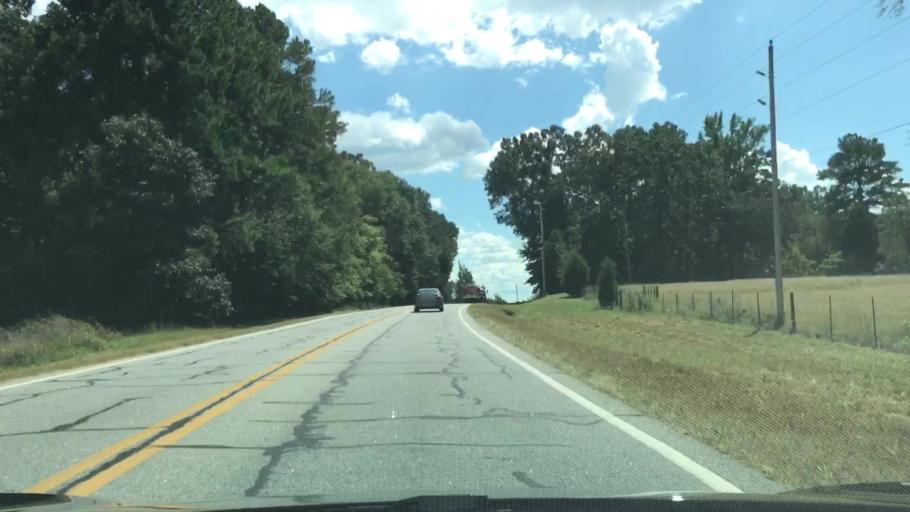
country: US
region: Georgia
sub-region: Oconee County
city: Watkinsville
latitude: 33.7497
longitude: -83.3013
